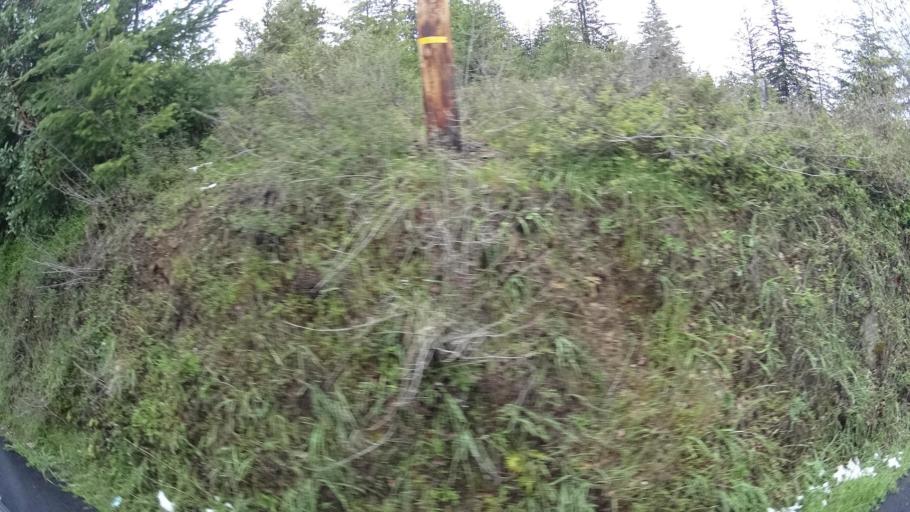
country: US
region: California
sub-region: Humboldt County
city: Blue Lake
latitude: 40.8736
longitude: -123.8864
